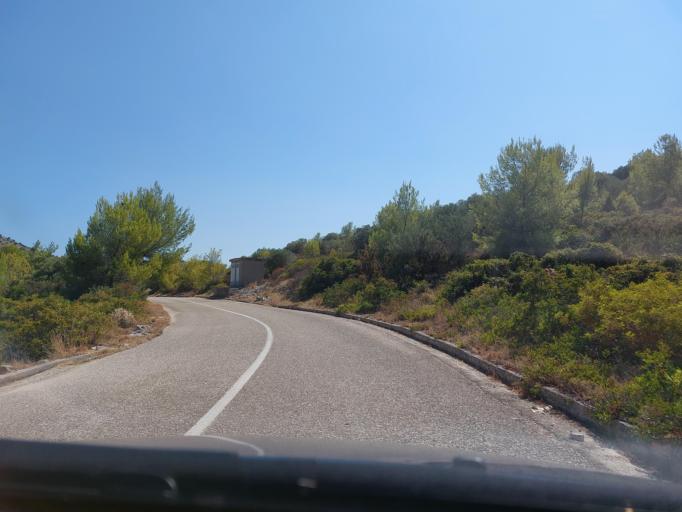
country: HR
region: Dubrovacko-Neretvanska
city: Smokvica
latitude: 42.7365
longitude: 16.8849
